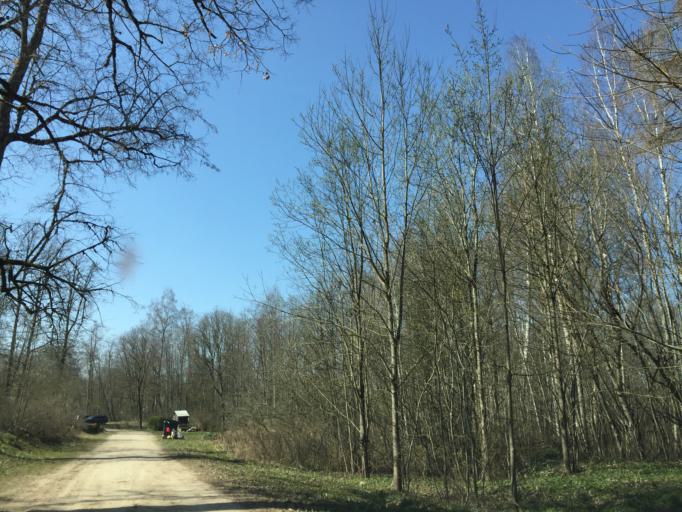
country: LV
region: Malpils
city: Malpils
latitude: 57.0081
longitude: 24.9694
